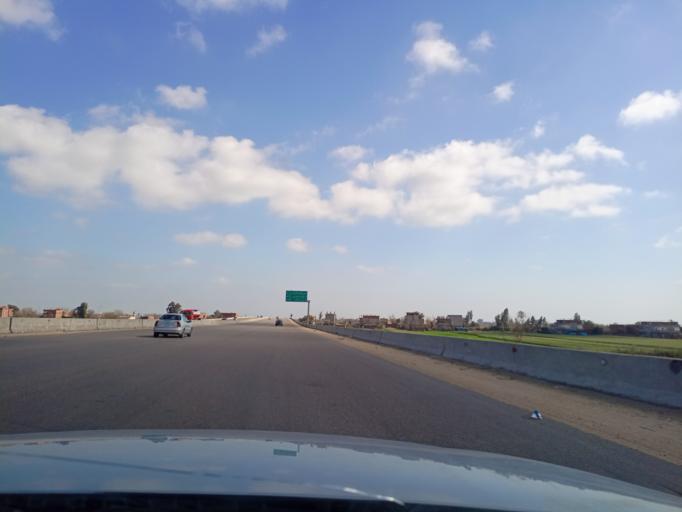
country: EG
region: Muhafazat al Minufiyah
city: Al Bajur
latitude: 30.3955
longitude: 31.0085
